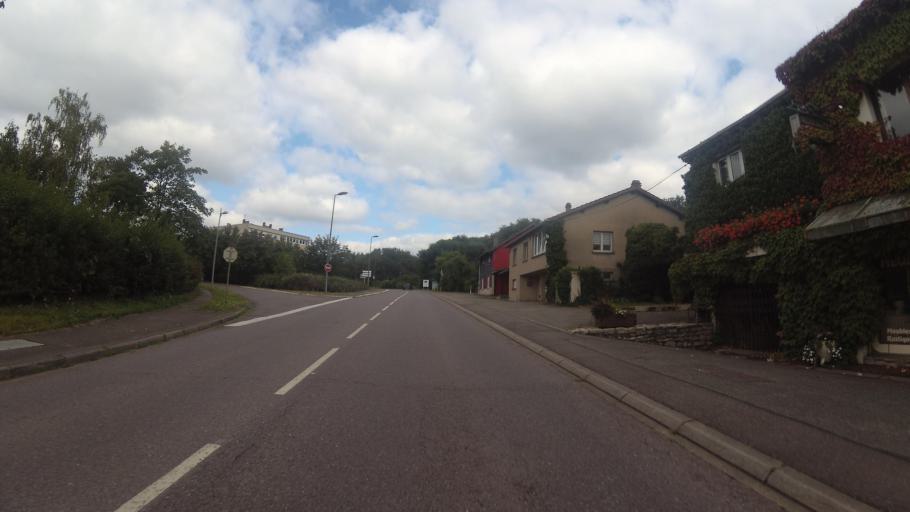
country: FR
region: Lorraine
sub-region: Departement de la Moselle
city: Creutzwald
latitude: 49.2104
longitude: 6.7147
